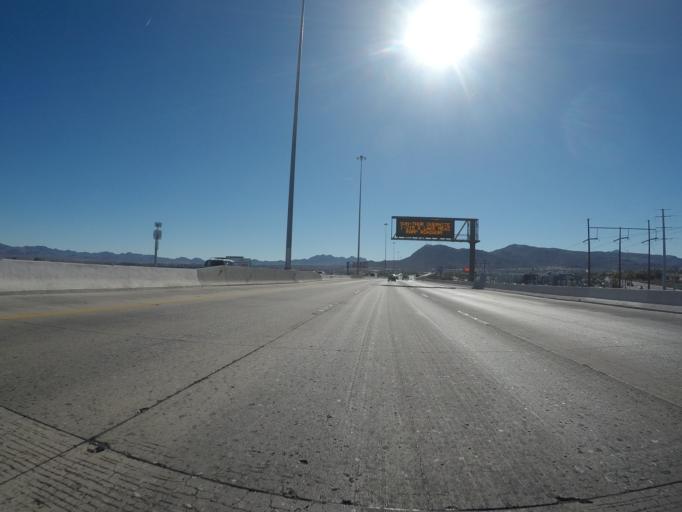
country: US
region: Nevada
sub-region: Clark County
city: Henderson
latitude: 36.0576
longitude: -115.0282
